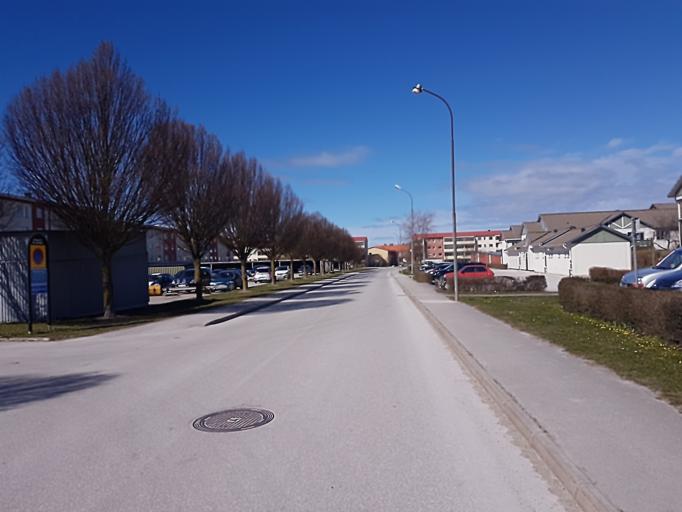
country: SE
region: Gotland
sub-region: Gotland
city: Visby
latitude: 57.6400
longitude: 18.3167
